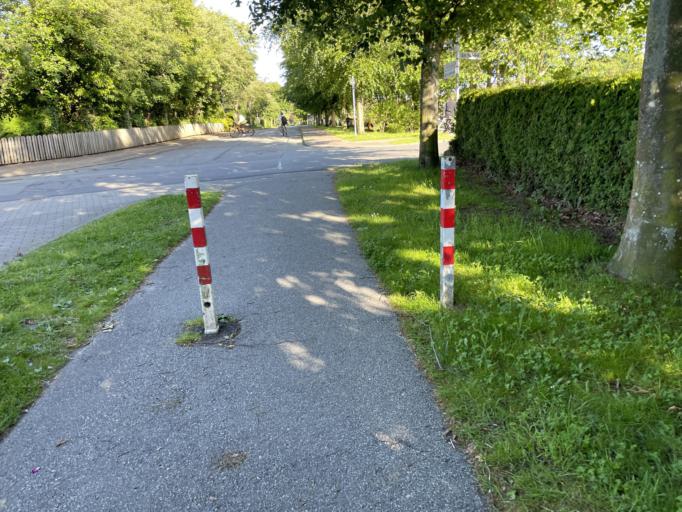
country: DE
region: Schleswig-Holstein
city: Mildstedt
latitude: 54.4639
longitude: 9.0988
